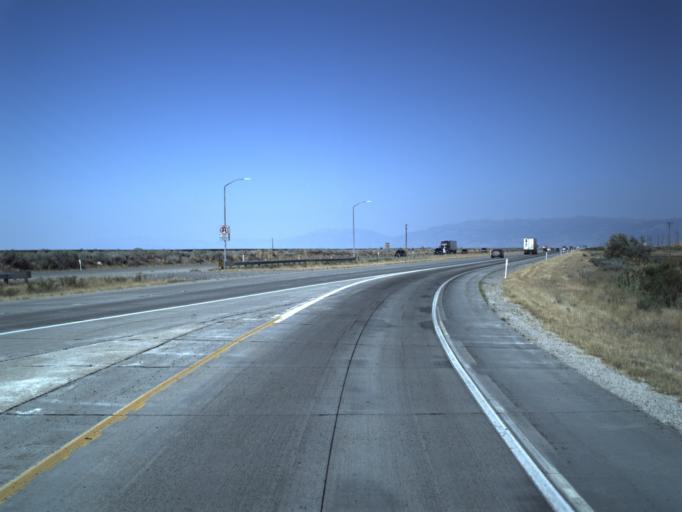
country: US
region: Utah
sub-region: Salt Lake County
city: Magna
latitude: 40.7483
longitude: -112.1790
